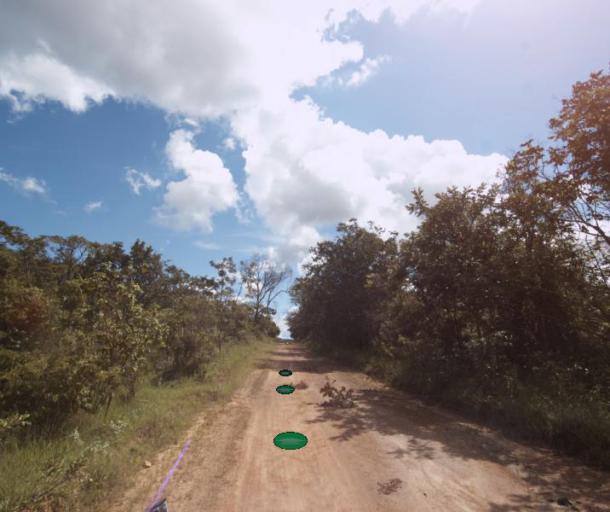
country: BR
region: Goias
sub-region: Pirenopolis
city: Pirenopolis
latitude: -15.7921
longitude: -48.8934
